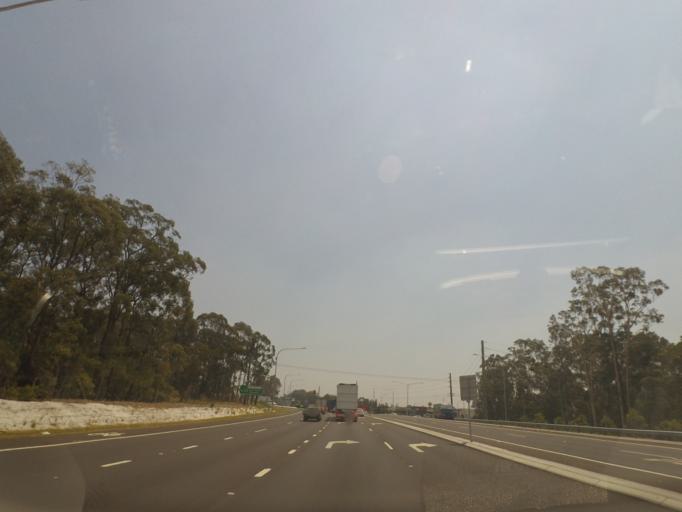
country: AU
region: New South Wales
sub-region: Newcastle
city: Beresfield
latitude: -32.8153
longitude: 151.6357
